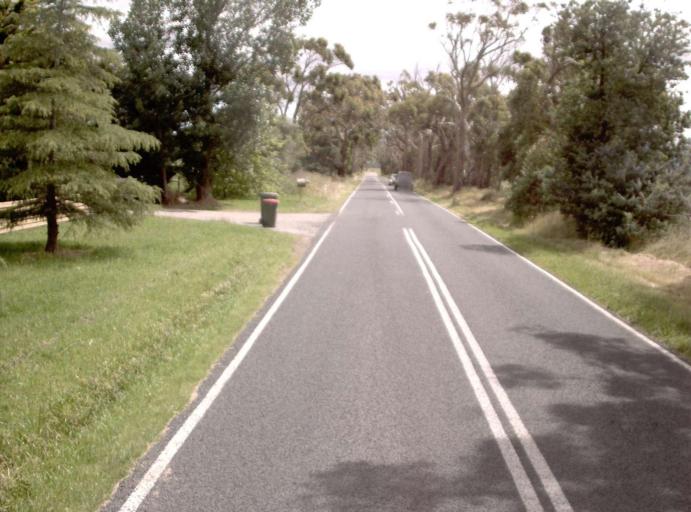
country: AU
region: Victoria
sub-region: Latrobe
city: Moe
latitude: -38.1177
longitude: 146.1491
